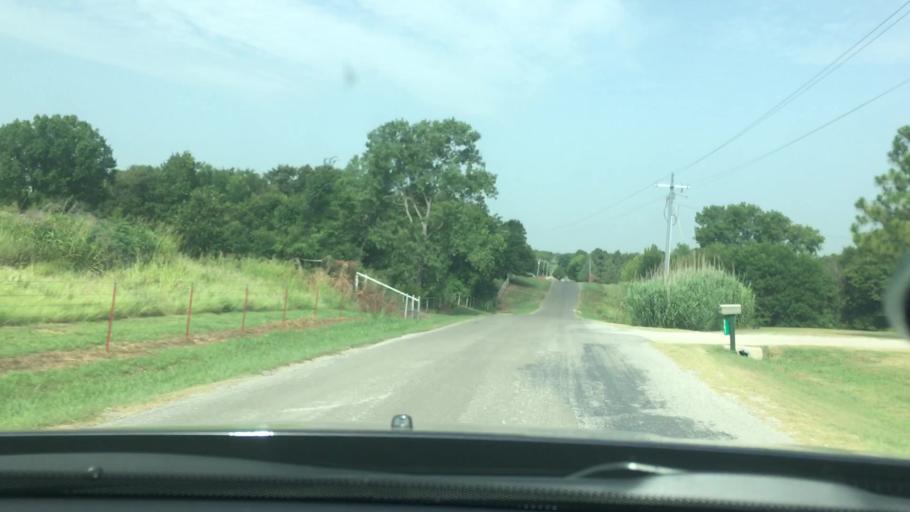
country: US
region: Oklahoma
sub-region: Garvin County
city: Pauls Valley
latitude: 34.7968
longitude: -97.1827
